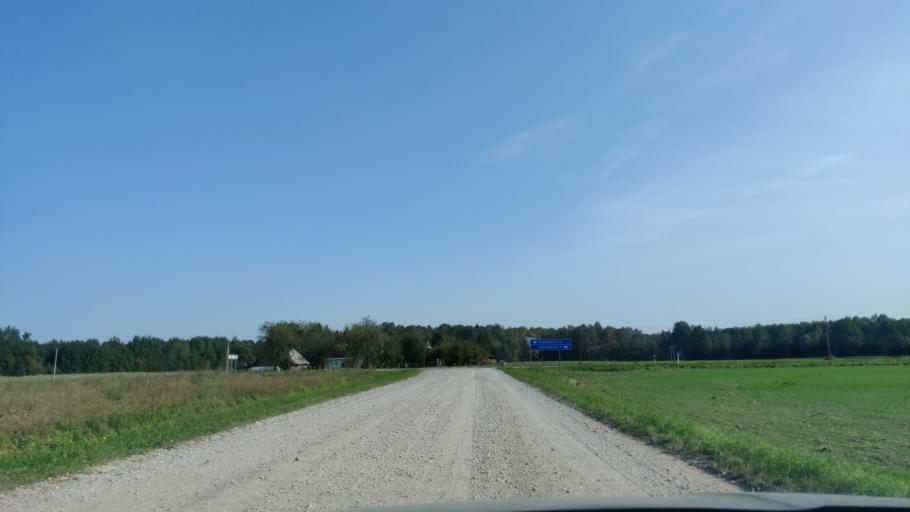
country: LT
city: Sirvintos
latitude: 54.9657
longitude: 24.8581
